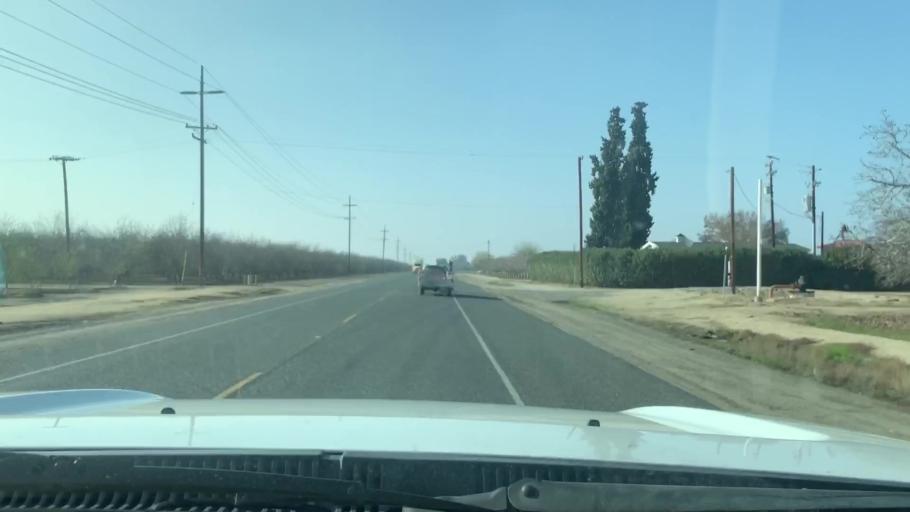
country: US
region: California
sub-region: Kern County
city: Wasco
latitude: 35.6015
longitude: -119.3709
